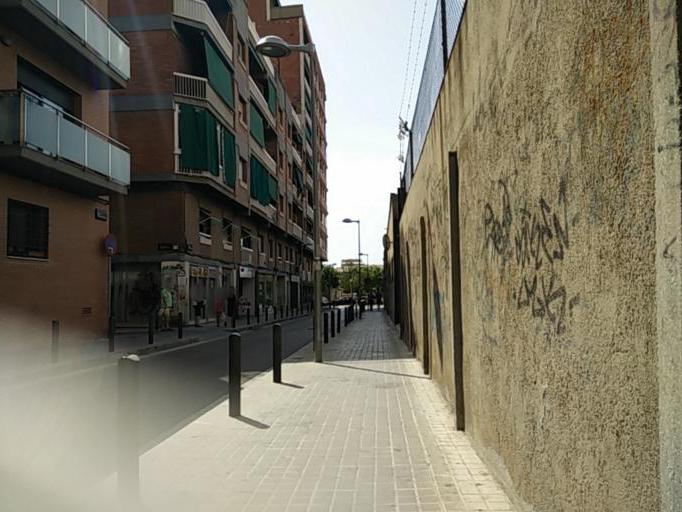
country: ES
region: Catalonia
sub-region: Provincia de Barcelona
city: Badalona
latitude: 41.4453
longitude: 2.2375
